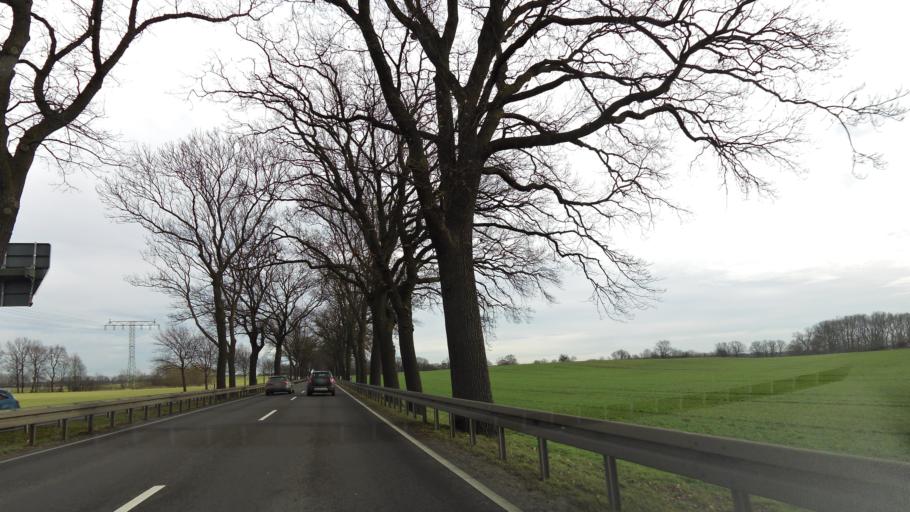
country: DE
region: Brandenburg
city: Schoneiche
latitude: 52.5007
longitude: 13.7053
